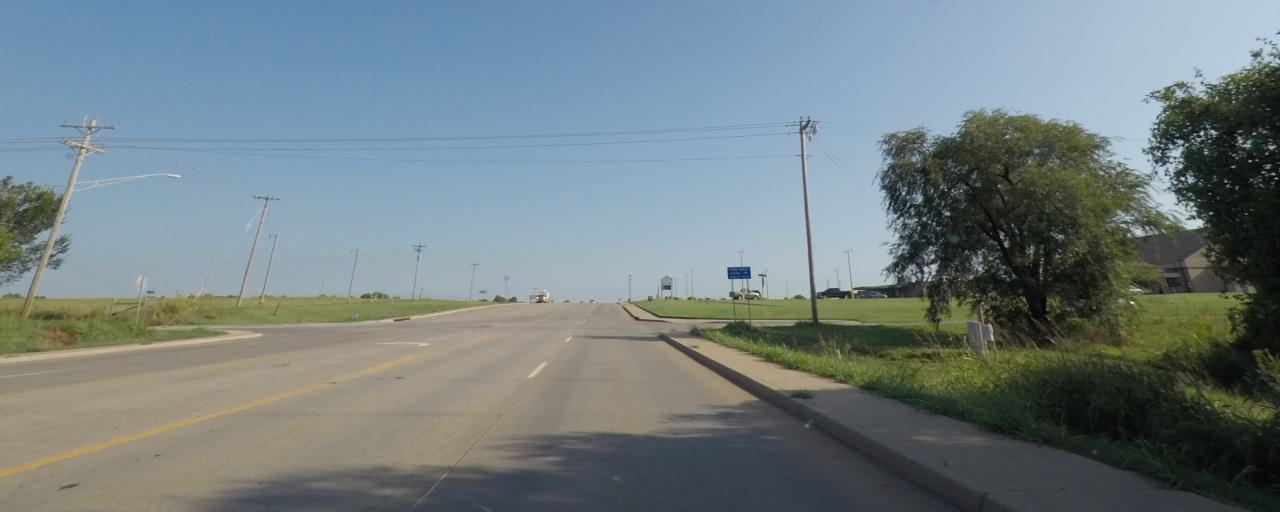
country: US
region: Oklahoma
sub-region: McClain County
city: Newcastle
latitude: 35.2615
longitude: -97.6001
